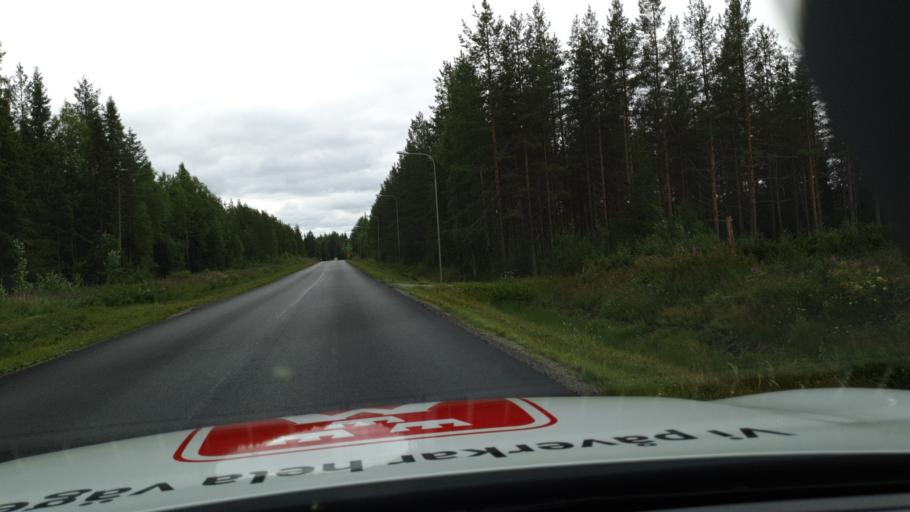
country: SE
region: Vaesterbotten
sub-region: Dorotea Kommun
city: Dorotea
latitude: 64.0746
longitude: 16.0843
